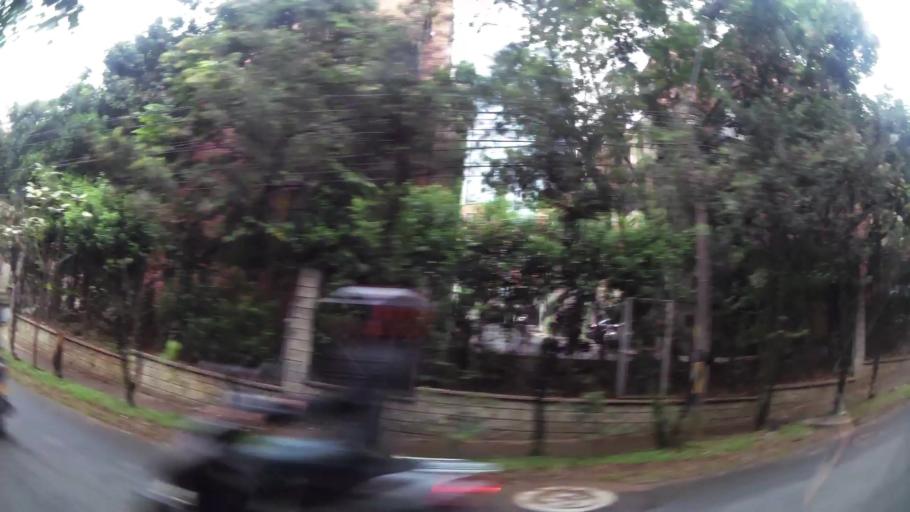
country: CO
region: Antioquia
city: Medellin
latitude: 6.2174
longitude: -75.5718
